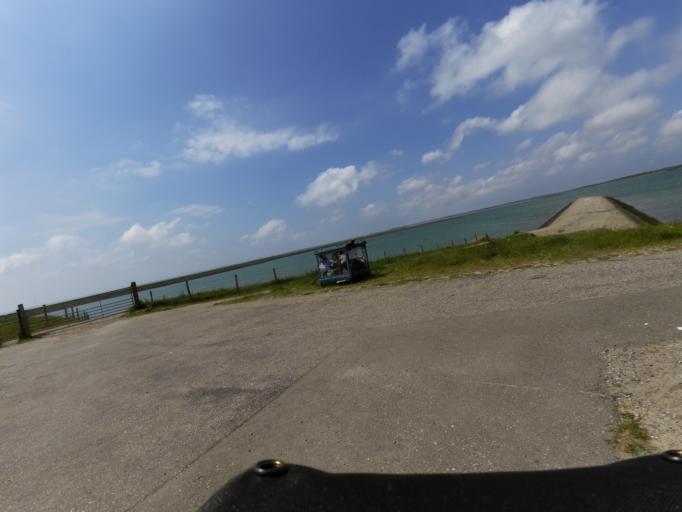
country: NL
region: Zeeland
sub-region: Schouwen-Duiveland
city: Scharendijke
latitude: 51.6869
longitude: 3.8255
